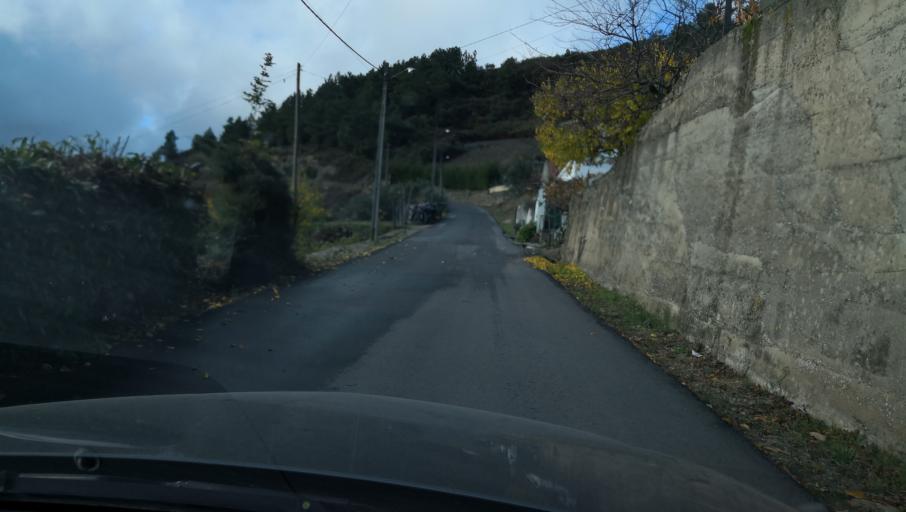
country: PT
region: Vila Real
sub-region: Sabrosa
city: Vilela
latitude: 41.2212
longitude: -7.5749
